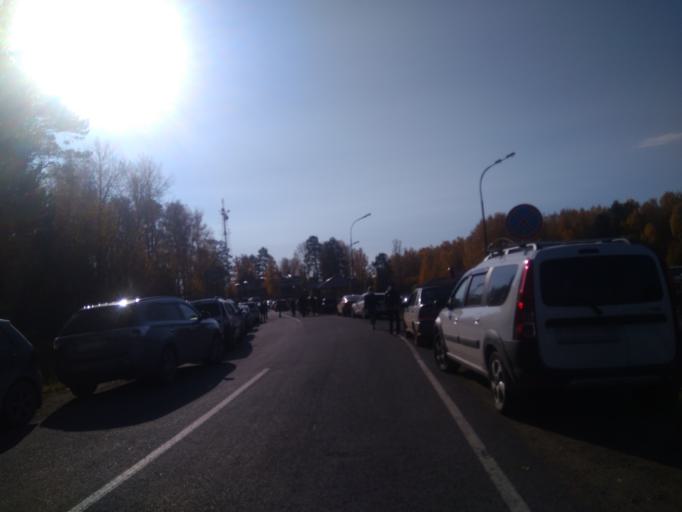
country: RU
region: Sverdlovsk
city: Mikhaylovsk
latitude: 56.5268
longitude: 59.2260
